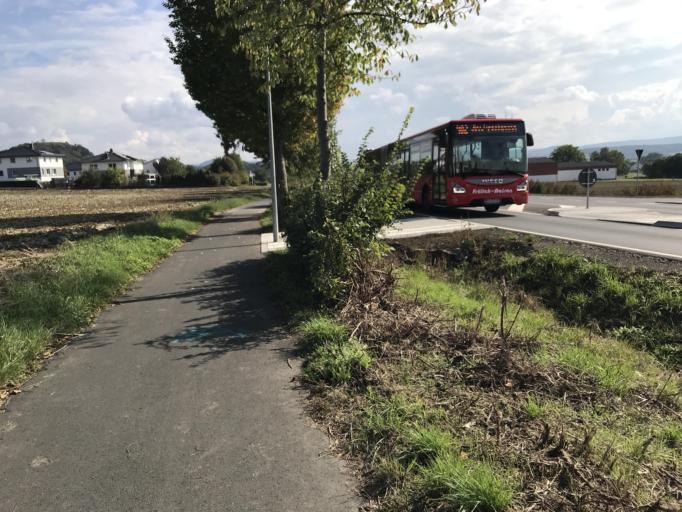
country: DE
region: Hesse
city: Gudensberg
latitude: 51.1712
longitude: 9.3668
